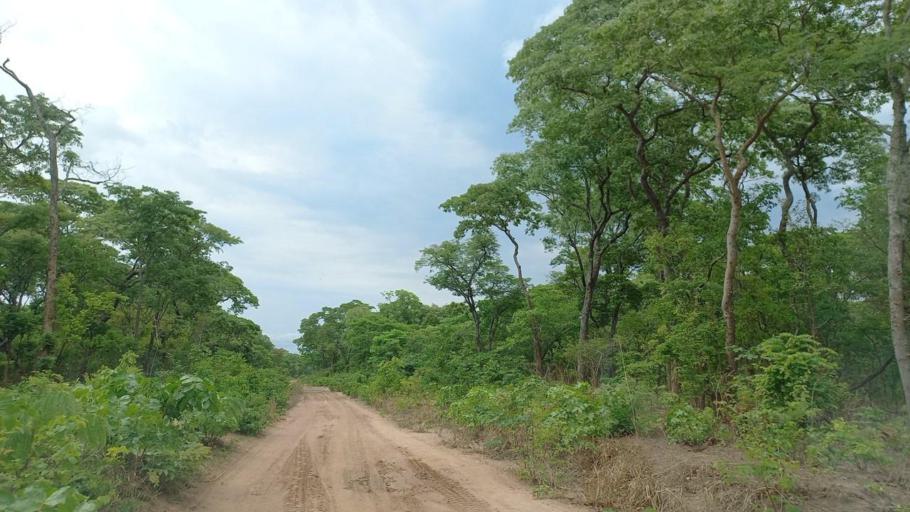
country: ZM
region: North-Western
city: Kalengwa
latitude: -13.5506
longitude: 24.9756
